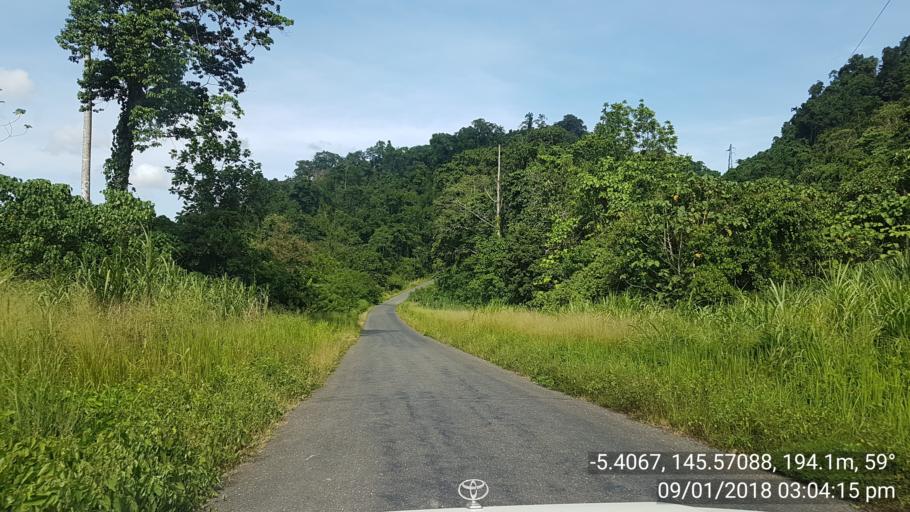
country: PG
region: Madang
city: Madang
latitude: -5.4066
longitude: 145.5709
